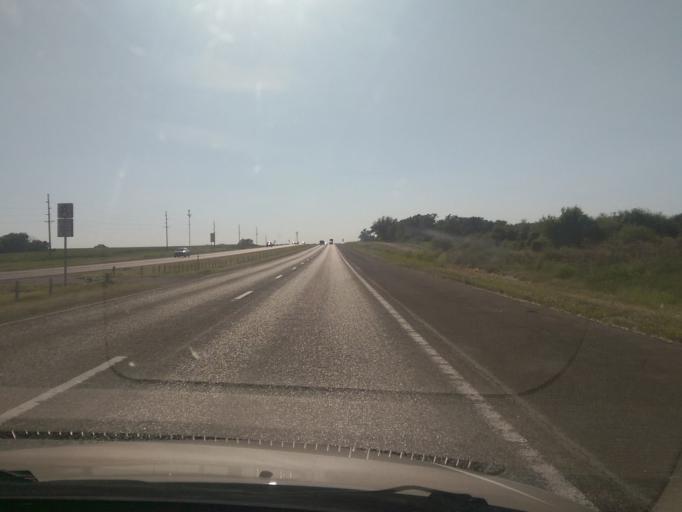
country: US
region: Missouri
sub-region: Lafayette County
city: Concordia
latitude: 38.9921
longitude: -93.6601
